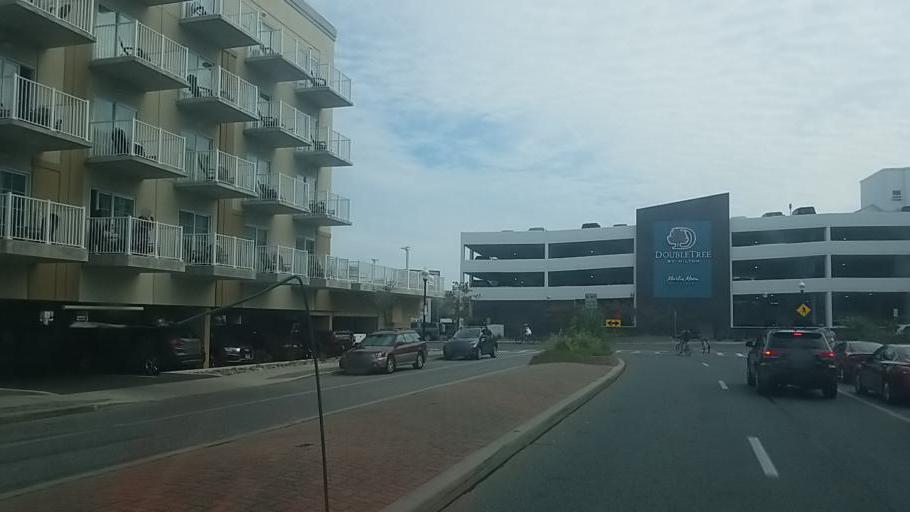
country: US
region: Maryland
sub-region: Worcester County
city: Ocean City
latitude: 38.3609
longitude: -75.0723
